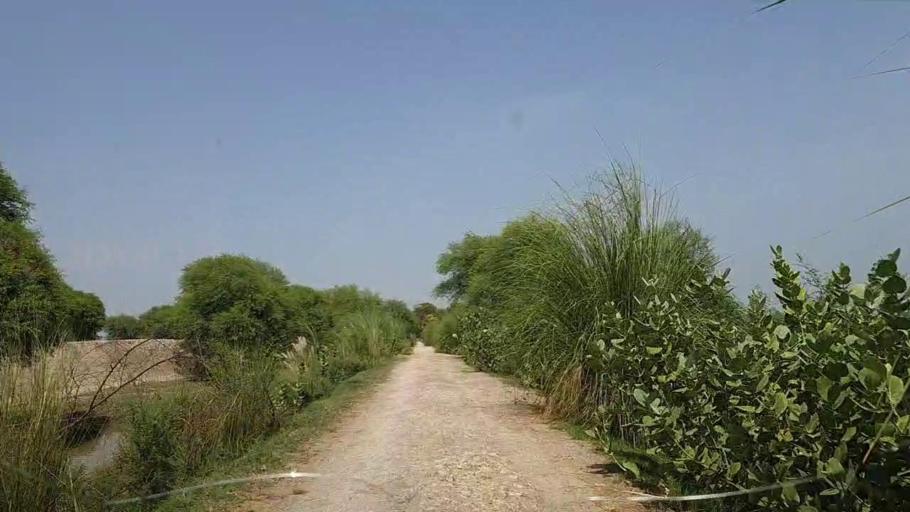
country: PK
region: Sindh
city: Ghotki
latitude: 28.0819
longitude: 69.3333
